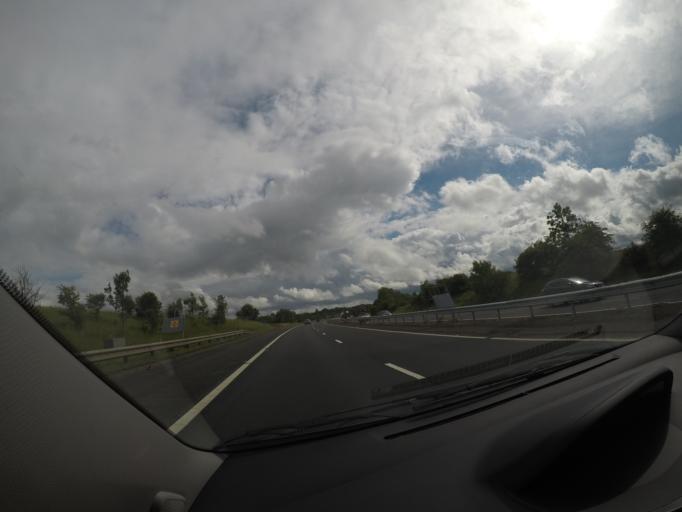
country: GB
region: Scotland
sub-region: North Lanarkshire
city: Glenboig
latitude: 55.8989
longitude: -4.0676
